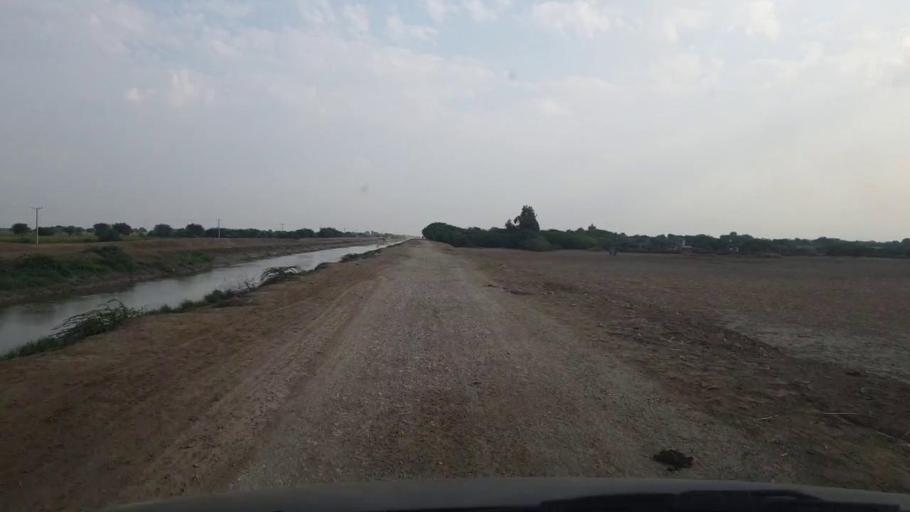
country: PK
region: Sindh
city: Badin
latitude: 24.5263
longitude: 68.6800
